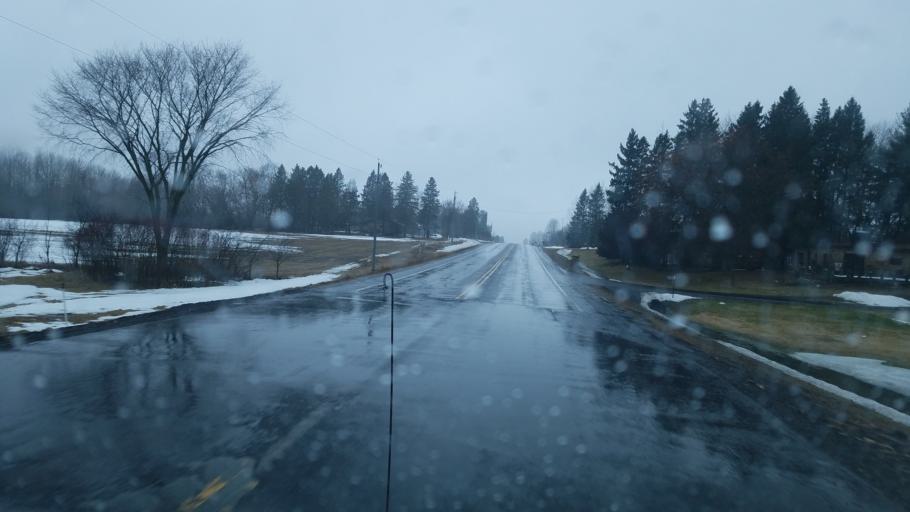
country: US
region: Wisconsin
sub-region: Marathon County
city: Spencer
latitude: 44.6778
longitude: -90.2615
